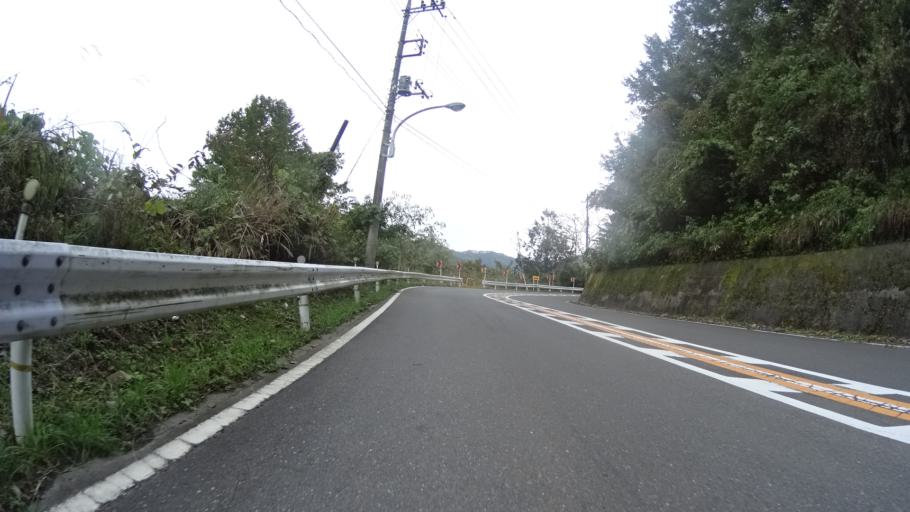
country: JP
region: Yamanashi
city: Uenohara
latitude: 35.6989
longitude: 139.1014
